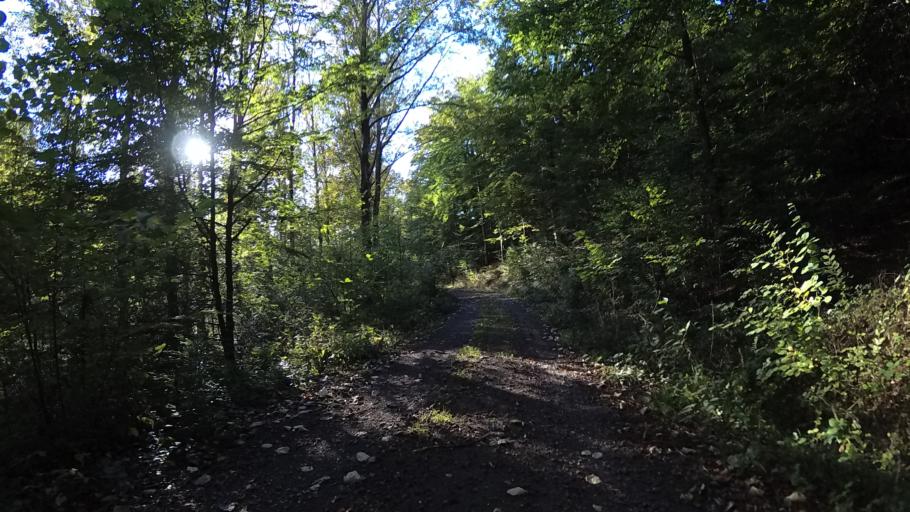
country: DE
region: Saarland
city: Ottweiler
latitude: 49.4291
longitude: 7.1919
